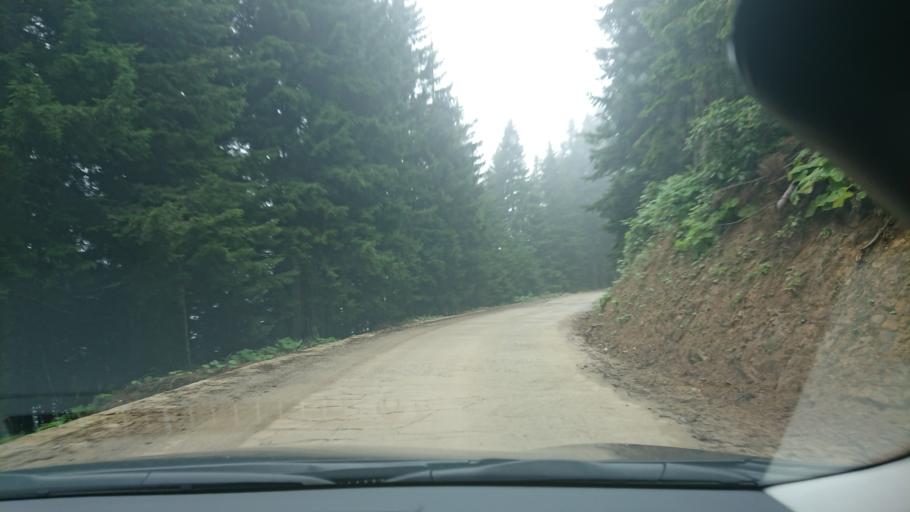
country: TR
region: Gumushane
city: Kurtun
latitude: 40.6691
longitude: 39.0117
